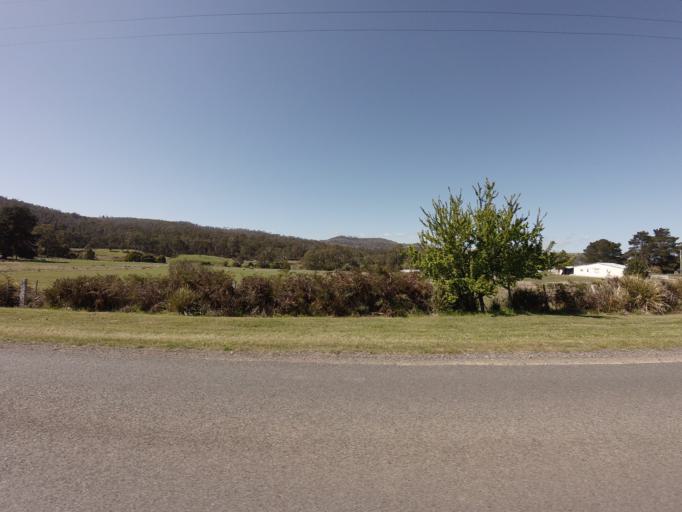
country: AU
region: Tasmania
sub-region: Derwent Valley
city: New Norfolk
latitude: -42.6686
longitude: 146.7899
